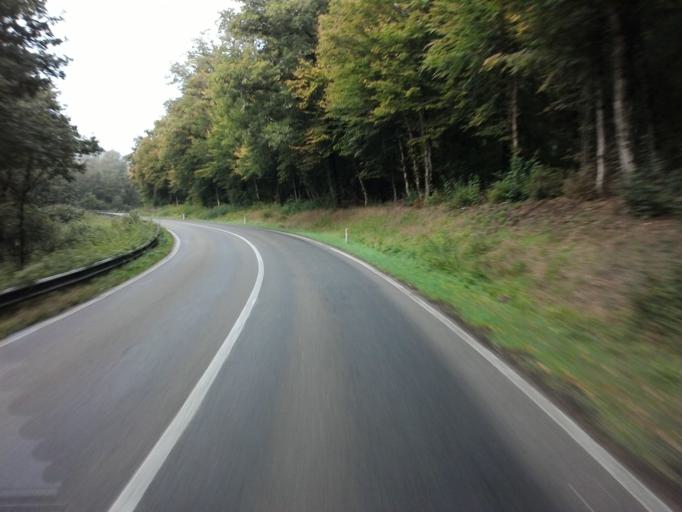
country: BE
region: Wallonia
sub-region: Province du Luxembourg
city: Saint-Leger
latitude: 49.5907
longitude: 5.6289
